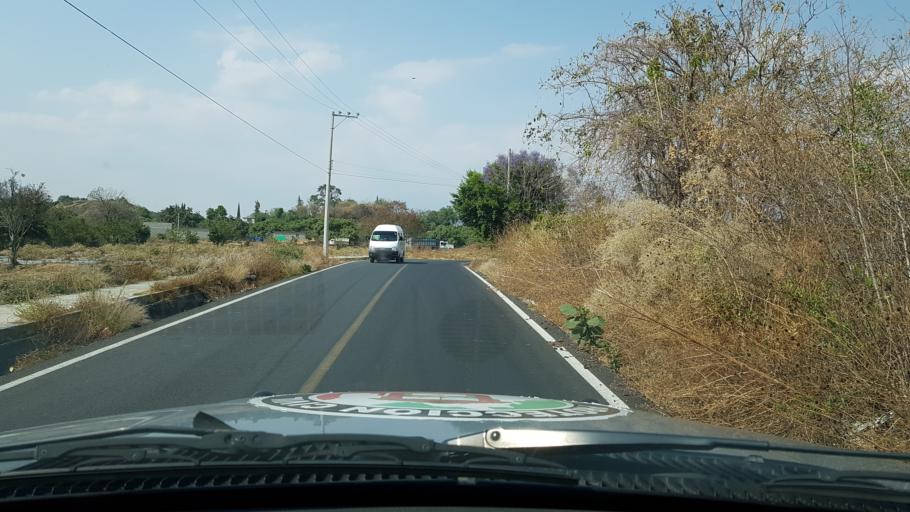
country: MX
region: Mexico
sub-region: Atlautla
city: San Andres Tlalamac
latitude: 18.9691
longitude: -98.8182
